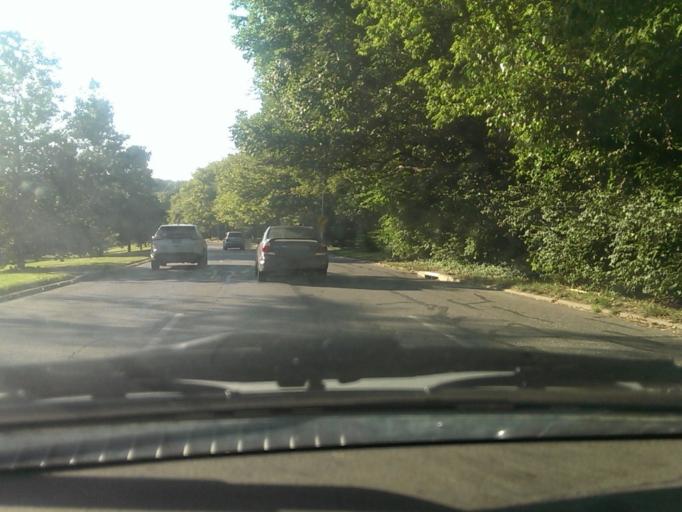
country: US
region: Kansas
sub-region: Johnson County
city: Westwood
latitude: 39.0292
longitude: -94.6036
